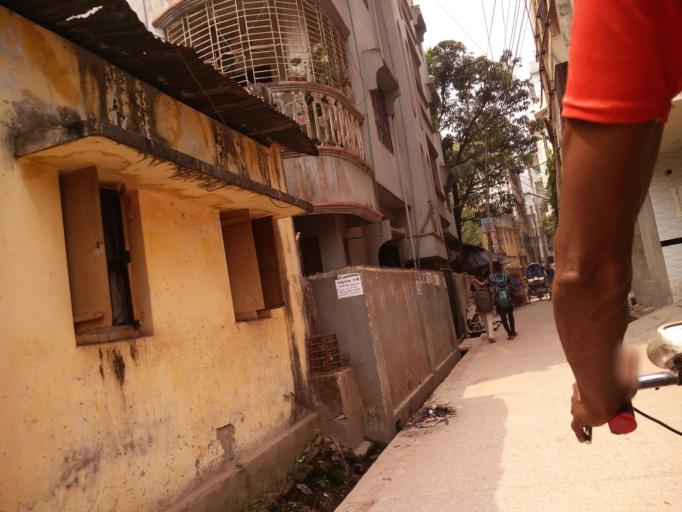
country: BD
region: Dhaka
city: Mymensingh
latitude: 24.7532
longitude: 90.4025
